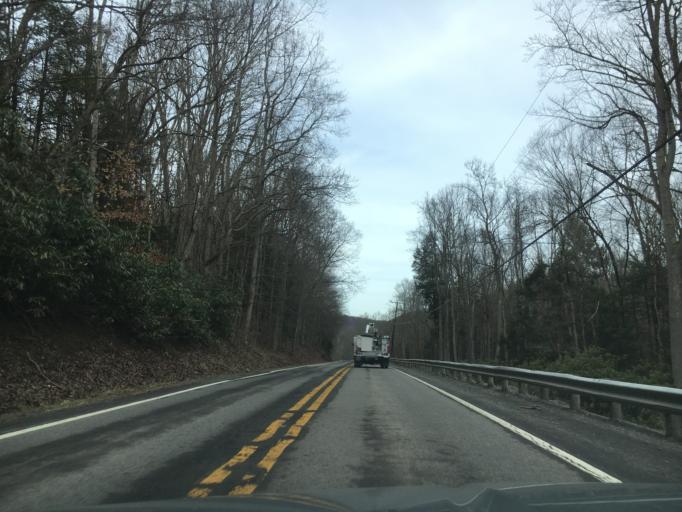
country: US
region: West Virginia
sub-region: Greenbrier County
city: Rainelle
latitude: 38.0411
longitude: -80.9228
